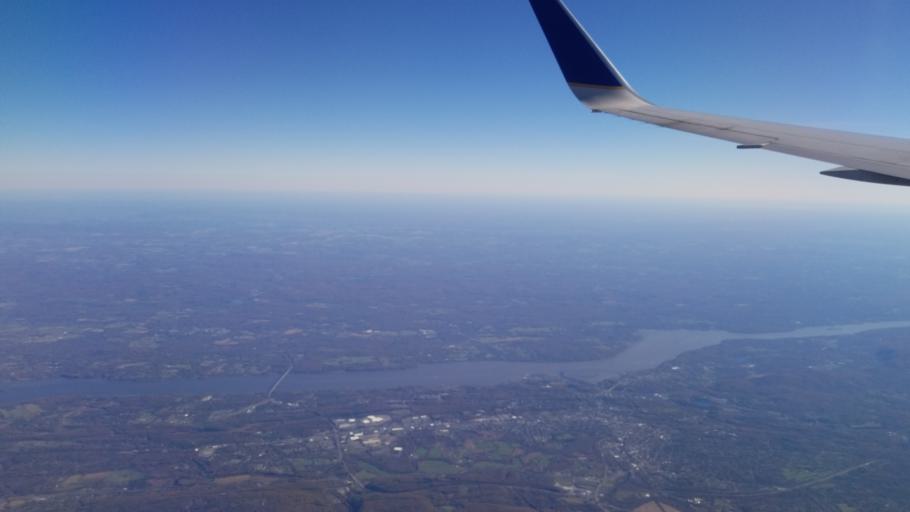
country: US
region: New York
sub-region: Ulster County
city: West Hurley
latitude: 42.0018
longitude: -74.1345
